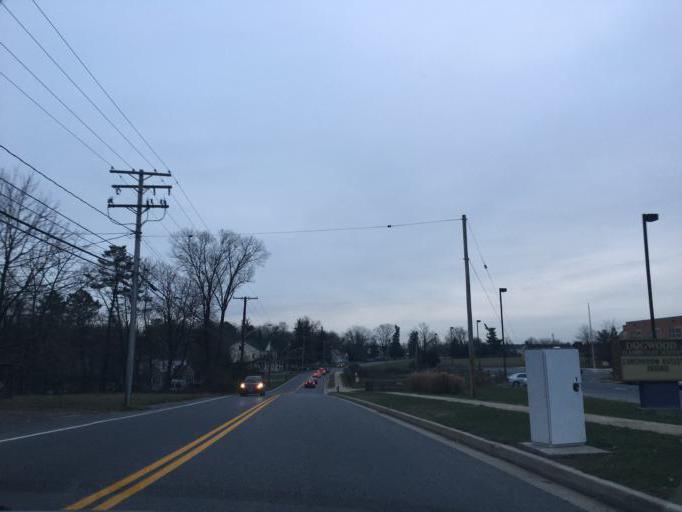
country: US
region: Maryland
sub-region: Baltimore County
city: Milford Mill
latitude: 39.3207
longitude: -76.7647
